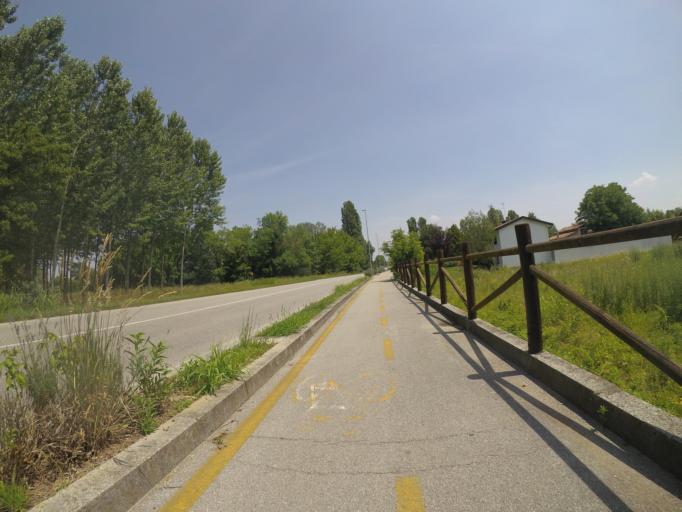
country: IT
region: Friuli Venezia Giulia
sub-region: Provincia di Udine
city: Rivignano
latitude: 45.8822
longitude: 13.0542
